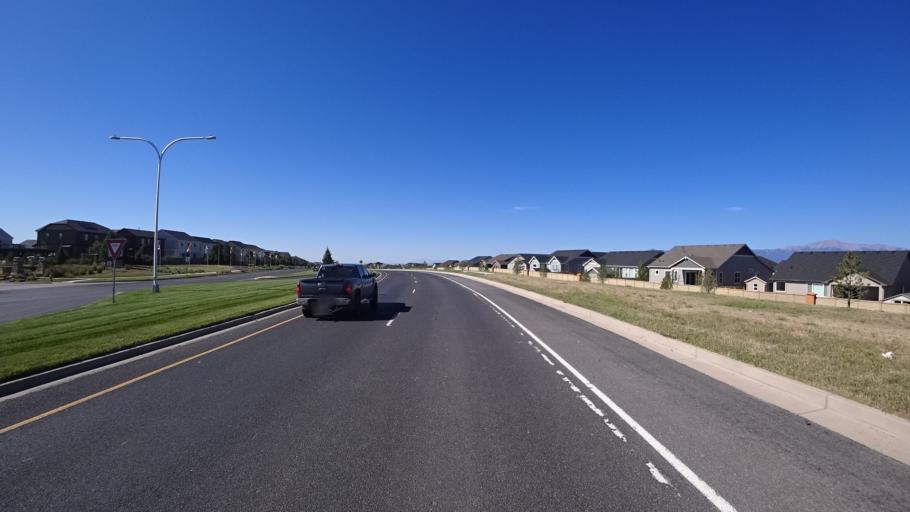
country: US
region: Colorado
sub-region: El Paso County
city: Cimarron Hills
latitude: 38.9348
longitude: -104.6828
